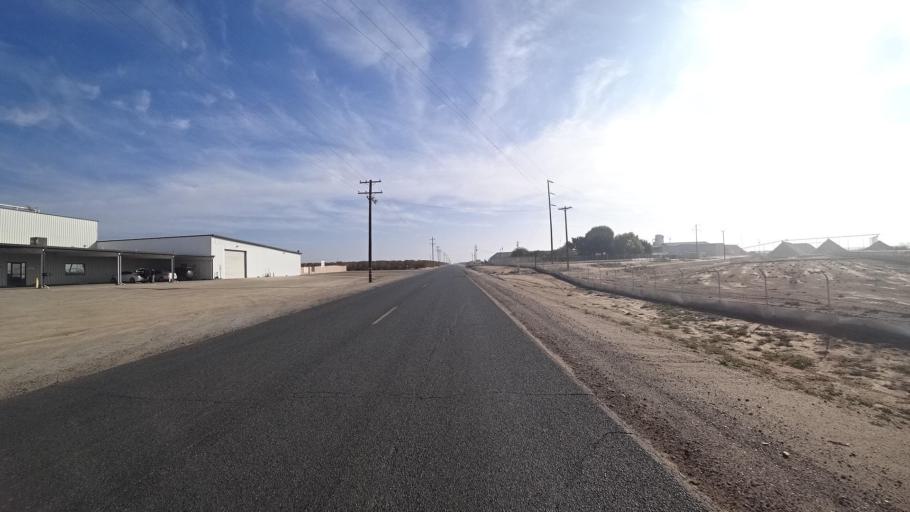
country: US
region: California
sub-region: Kern County
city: McFarland
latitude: 35.6020
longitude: -119.1945
